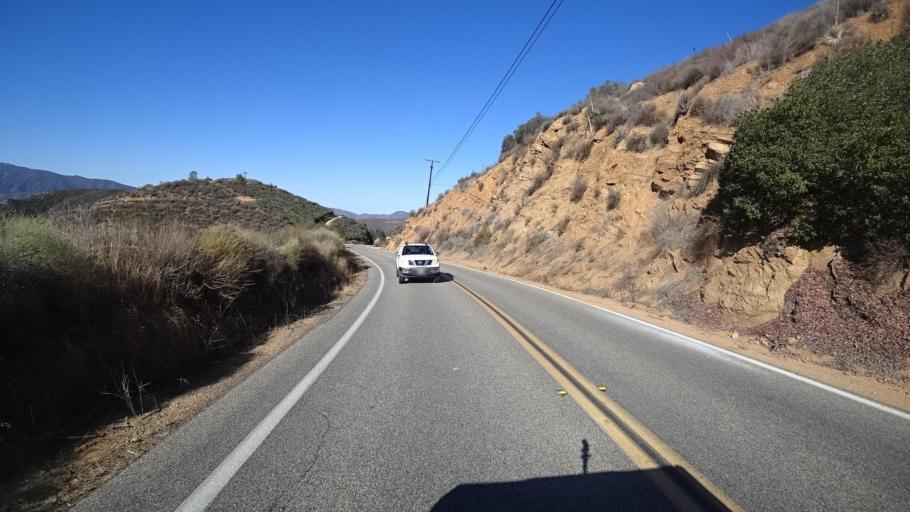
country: US
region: California
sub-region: San Diego County
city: Jamul
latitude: 32.6730
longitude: -116.7700
